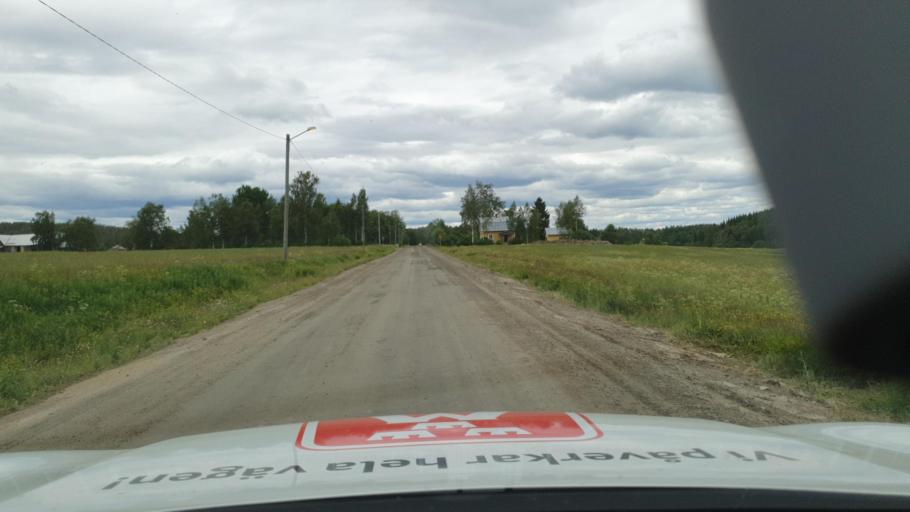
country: SE
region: Vaesterbotten
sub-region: Nordmalings Kommun
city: Nordmaling
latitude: 63.7086
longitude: 19.4345
